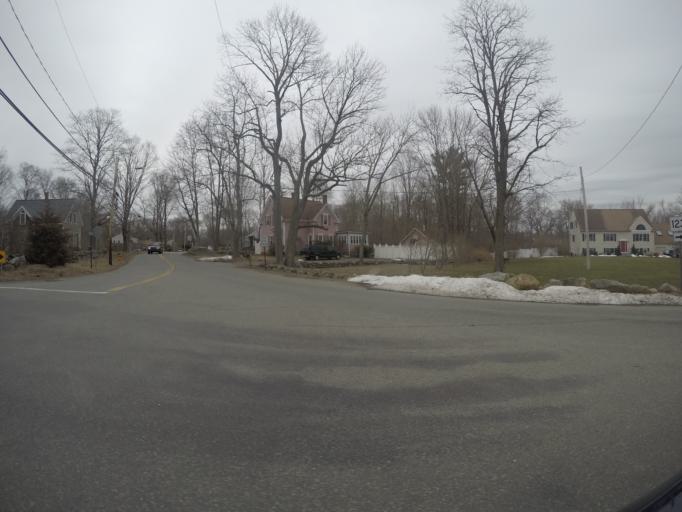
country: US
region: Massachusetts
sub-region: Bristol County
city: Easton
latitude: 42.0364
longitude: -71.0963
